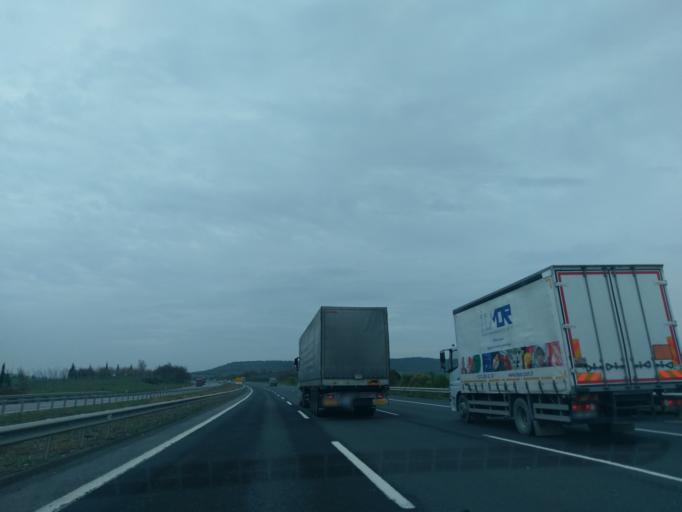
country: TR
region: Istanbul
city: Canta
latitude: 41.1548
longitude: 28.1423
